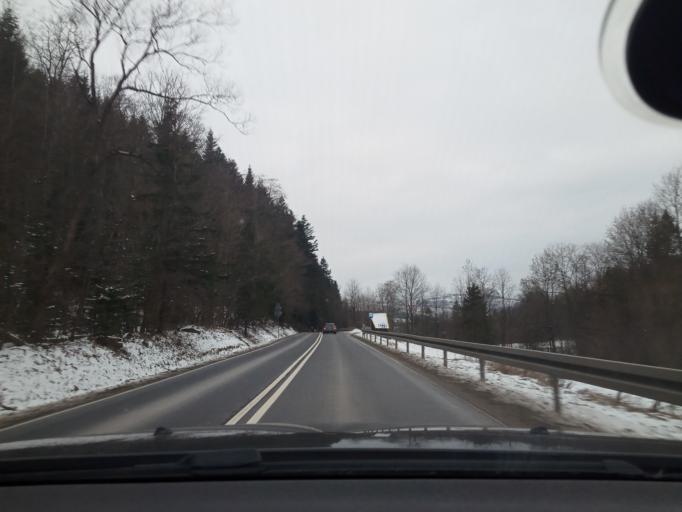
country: PL
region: Lesser Poland Voivodeship
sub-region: Powiat limanowski
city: Lubomierz
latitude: 49.6185
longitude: 20.1627
